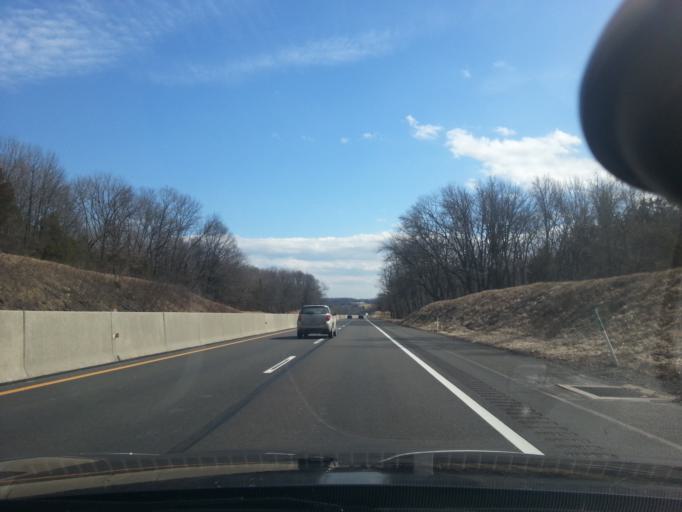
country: US
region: Pennsylvania
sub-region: Montgomery County
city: Telford
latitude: 40.3430
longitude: -75.3867
